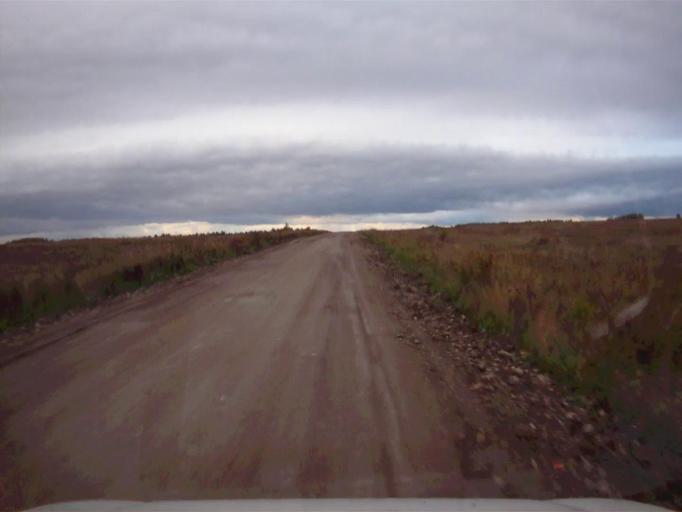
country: RU
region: Sverdlovsk
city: Mikhaylovsk
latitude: 56.1827
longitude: 59.1844
